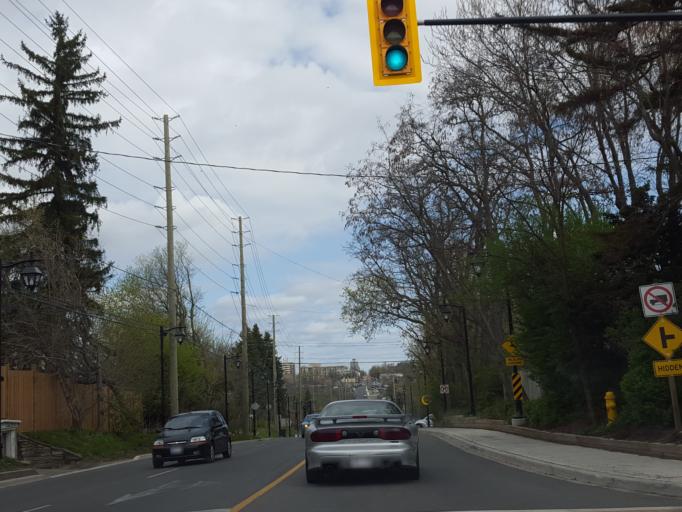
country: CA
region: Ontario
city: Markham
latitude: 43.8664
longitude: -79.2580
